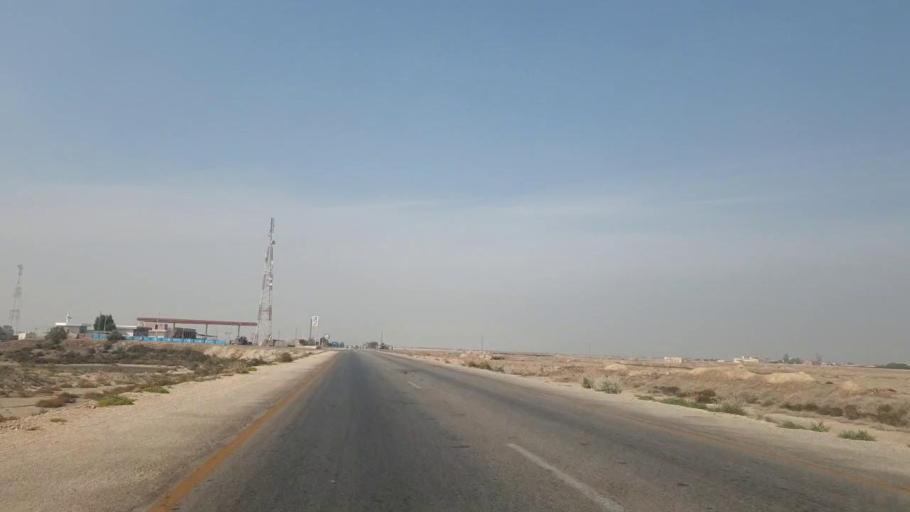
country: PK
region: Sindh
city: Sann
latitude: 25.8992
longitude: 68.2337
